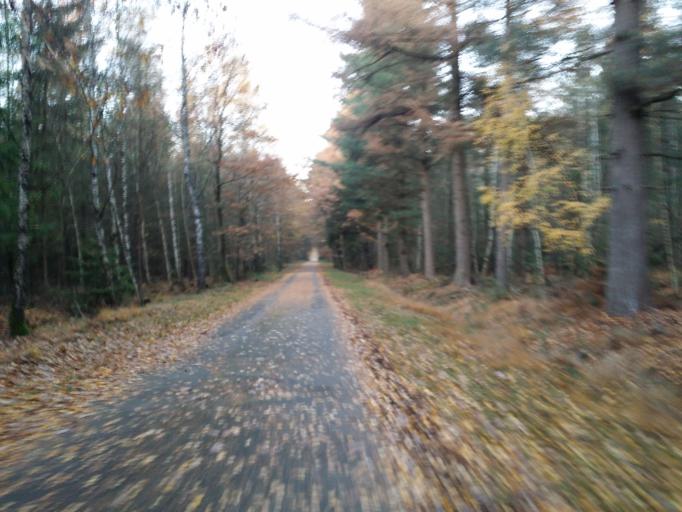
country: DE
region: Lower Saxony
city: Ahausen
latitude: 53.0941
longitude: 9.3164
